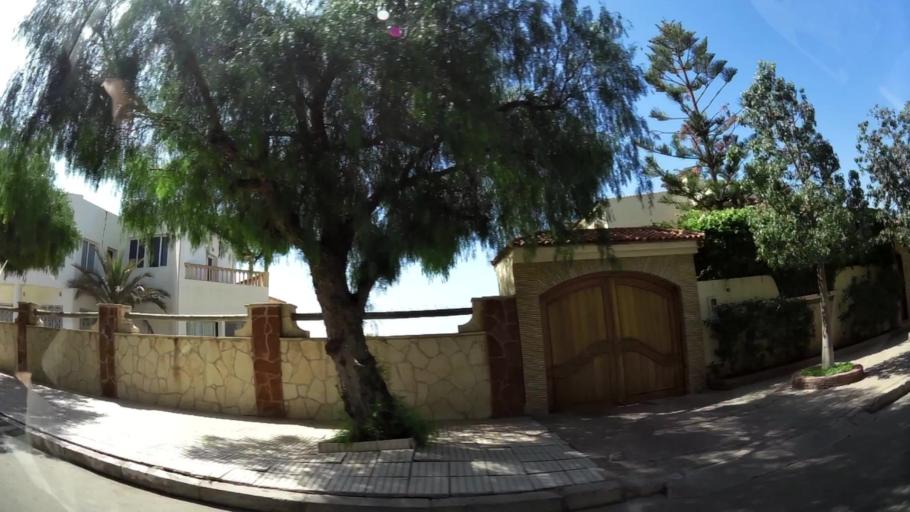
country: MA
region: Souss-Massa-Draa
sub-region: Agadir-Ida-ou-Tnan
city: Agadir
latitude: 30.4428
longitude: -9.5890
